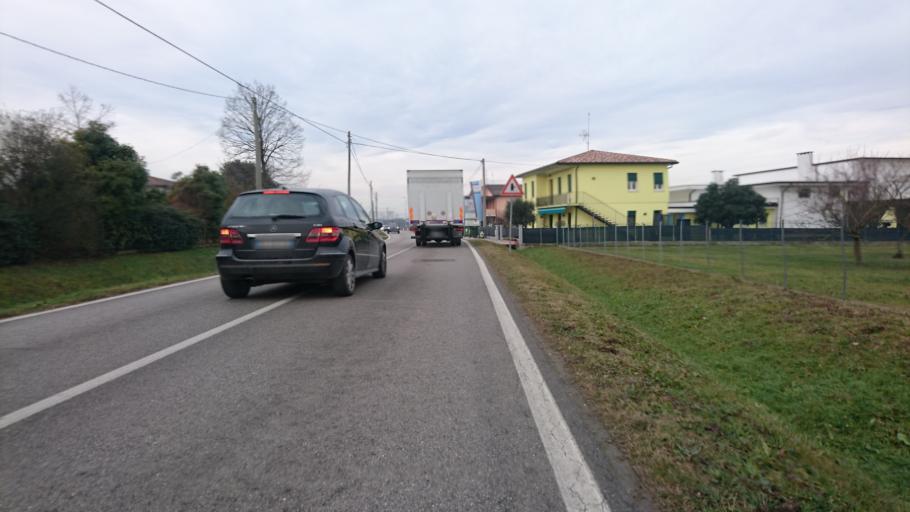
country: IT
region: Veneto
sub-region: Provincia di Padova
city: Ronchi di Campanile
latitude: 45.4705
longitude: 11.7895
